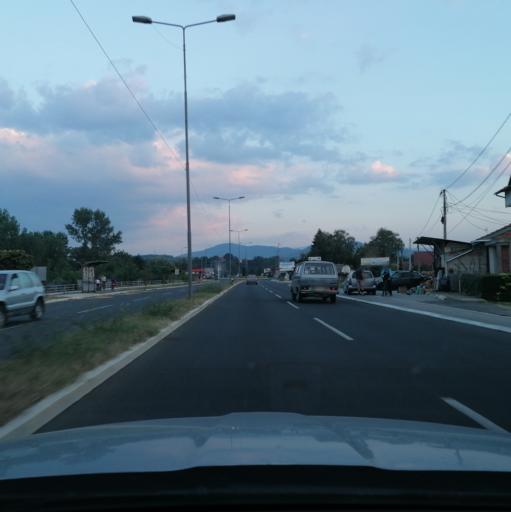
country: RS
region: Central Serbia
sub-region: Raski Okrug
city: Kraljevo
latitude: 43.7142
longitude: 20.6934
